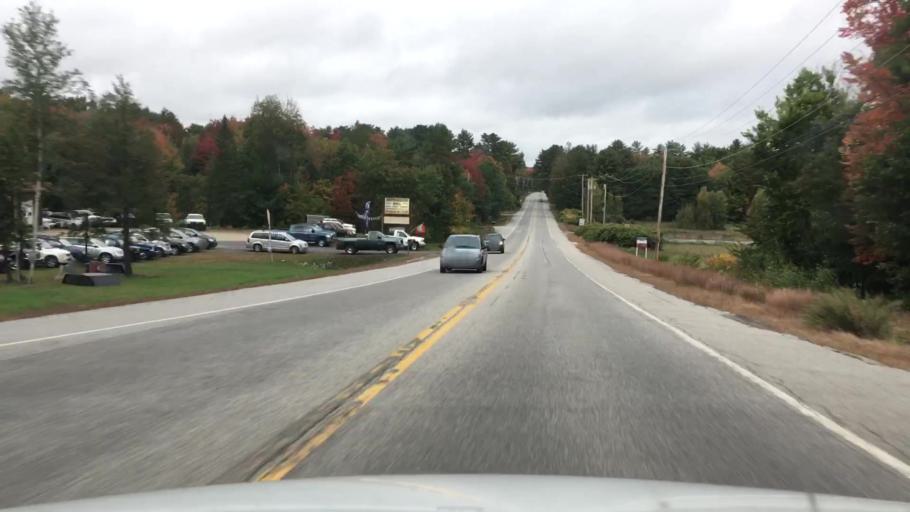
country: US
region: Maine
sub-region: Oxford County
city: Oxford
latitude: 44.1261
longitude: -70.4529
